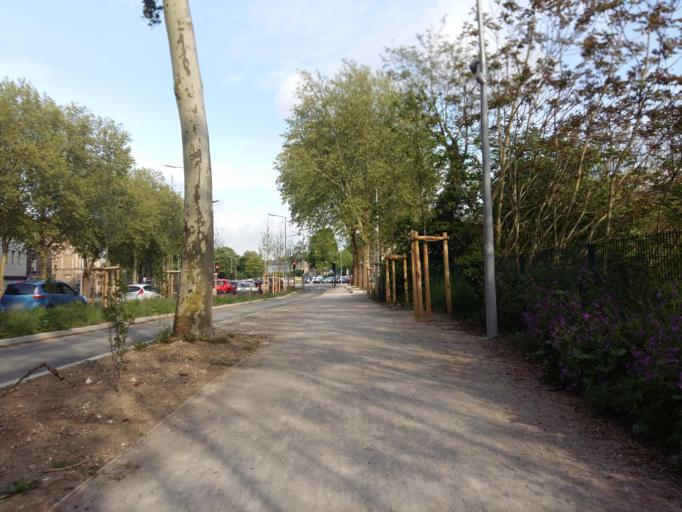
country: FR
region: Picardie
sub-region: Departement de la Somme
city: Amiens
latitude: 49.8893
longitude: 2.2935
